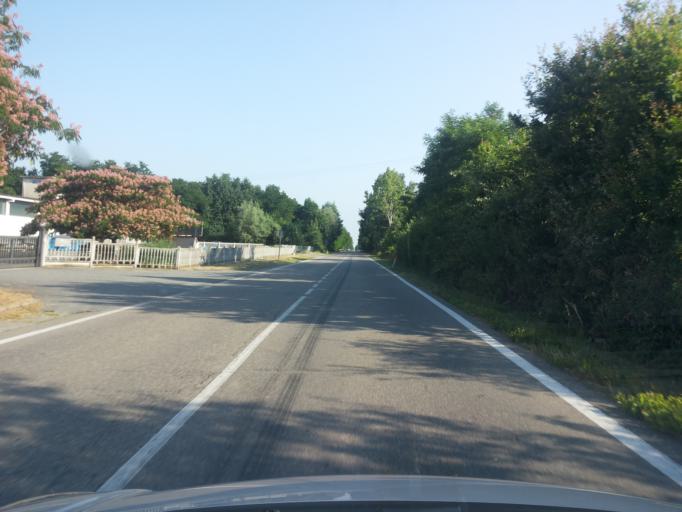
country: IT
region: Piedmont
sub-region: Provincia di Biella
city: Mottalciata
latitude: 45.4984
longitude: 8.2143
